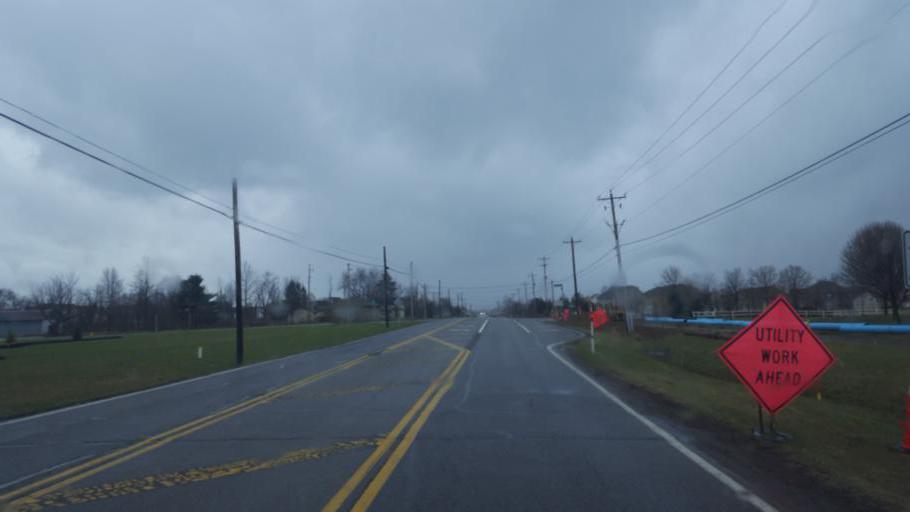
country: US
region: Ohio
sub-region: Delaware County
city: Lewis Center
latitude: 40.1625
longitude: -82.9930
